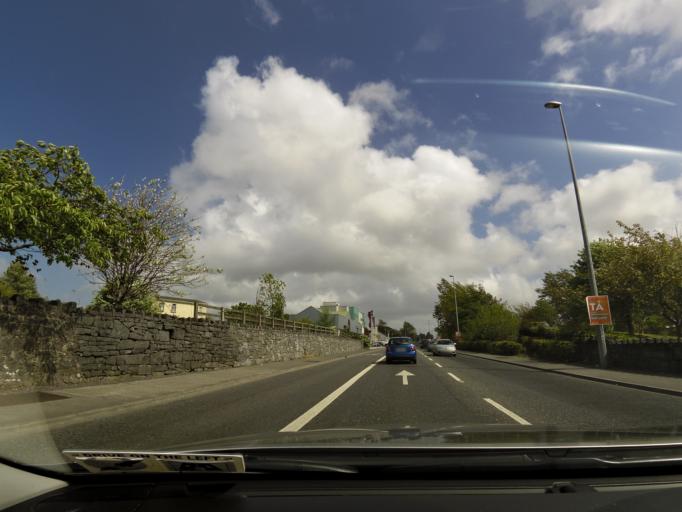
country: IE
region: Connaught
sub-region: County Galway
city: Gaillimh
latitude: 53.2806
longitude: -9.0288
